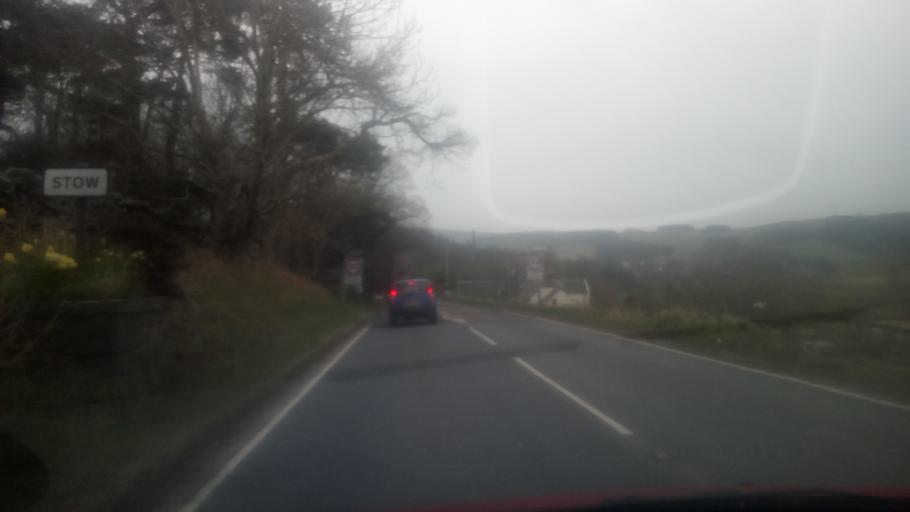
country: GB
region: Scotland
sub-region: The Scottish Borders
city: Galashiels
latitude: 55.6981
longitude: -2.8739
